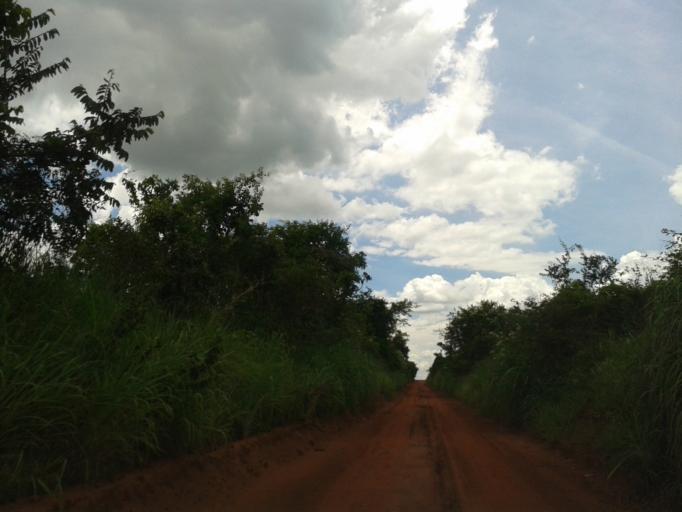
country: BR
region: Minas Gerais
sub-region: Ituiutaba
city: Ituiutaba
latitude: -18.8808
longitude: -49.4756
